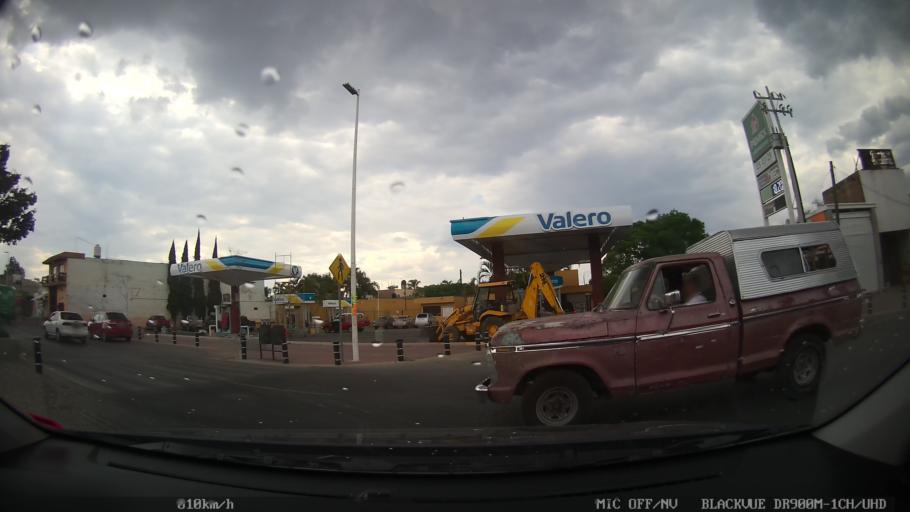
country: MX
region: Jalisco
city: Tonala
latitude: 20.6190
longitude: -103.2462
